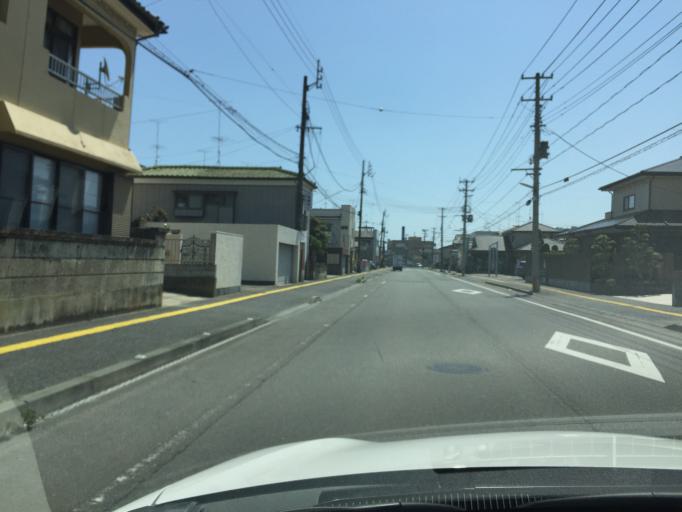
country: JP
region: Fukushima
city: Iwaki
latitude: 36.9567
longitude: 140.9012
